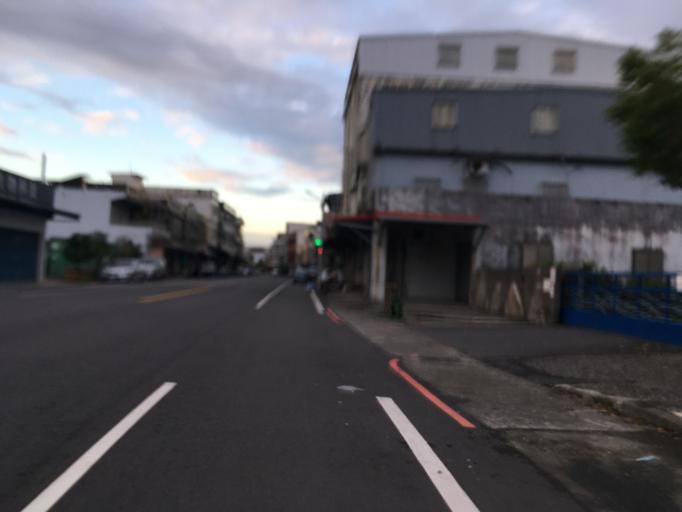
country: TW
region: Taiwan
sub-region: Yilan
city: Yilan
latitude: 24.6219
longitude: 121.8344
